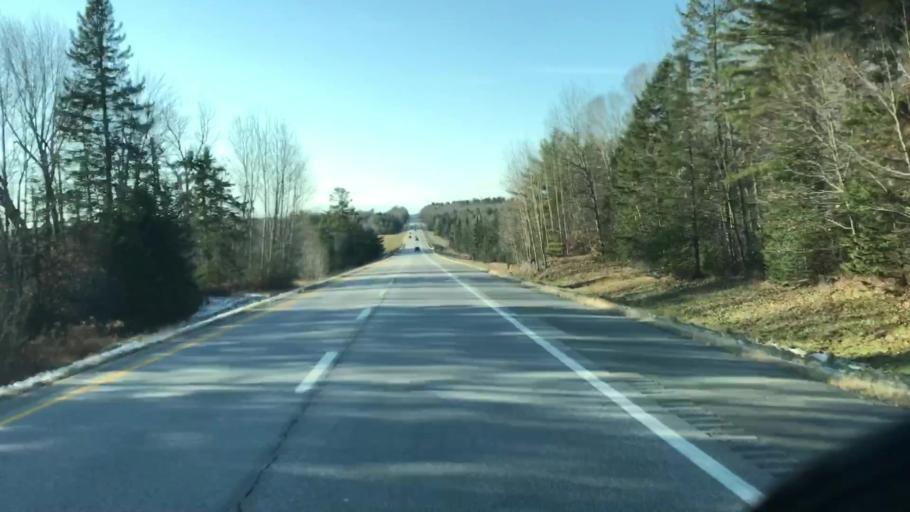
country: US
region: Maine
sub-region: Penobscot County
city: Carmel
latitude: 44.7754
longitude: -69.0388
